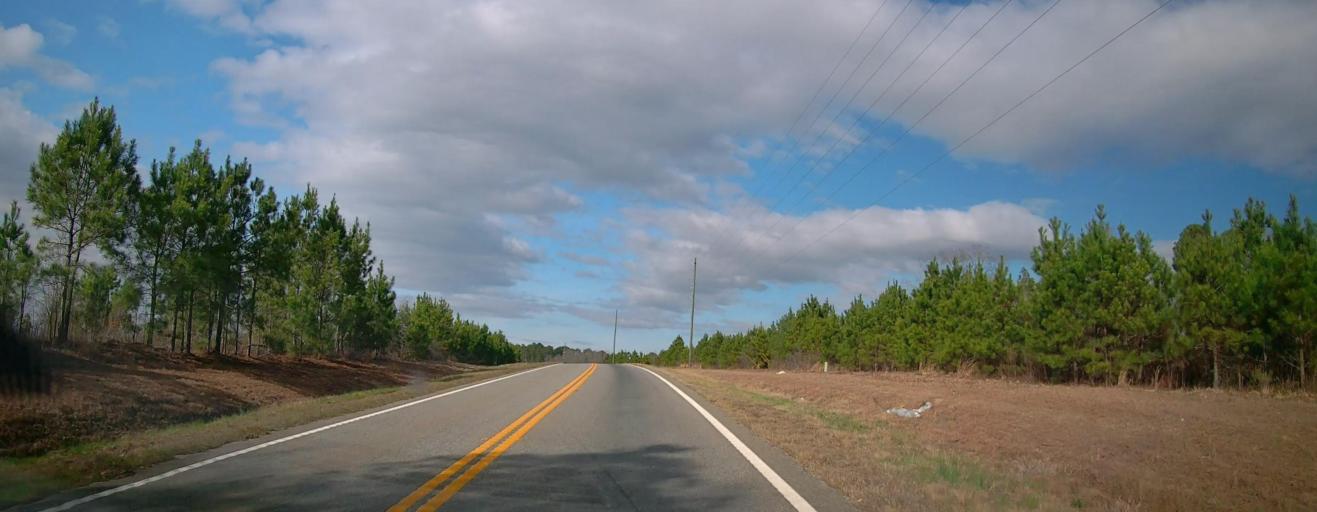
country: US
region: Georgia
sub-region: Taylor County
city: Butler
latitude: 32.4536
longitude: -84.3609
